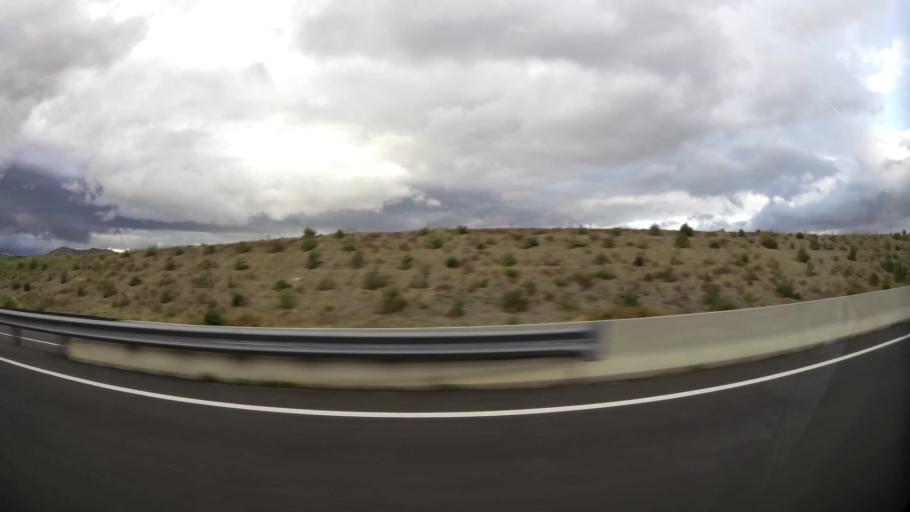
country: MA
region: Taza-Al Hoceima-Taounate
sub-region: Taza
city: Taza
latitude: 34.2538
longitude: -3.9275
